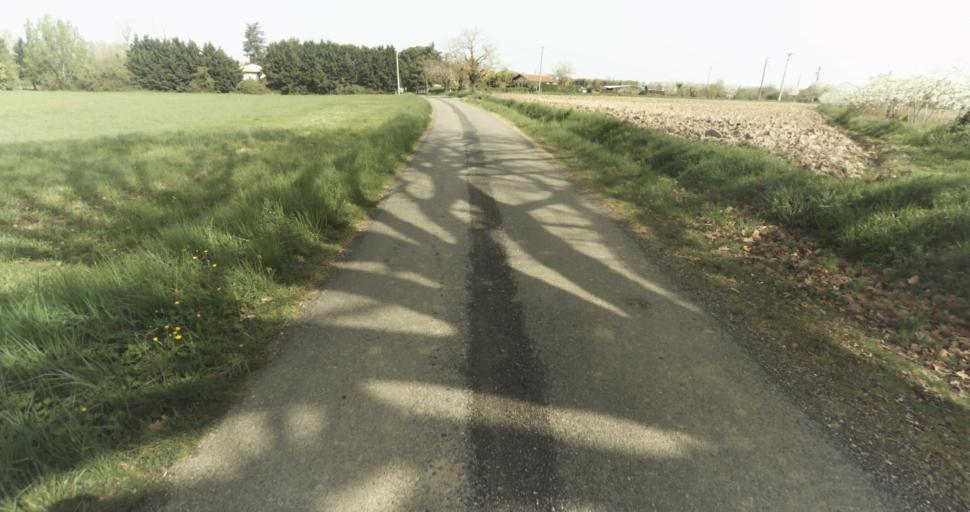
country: FR
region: Midi-Pyrenees
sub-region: Departement du Tarn-et-Garonne
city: Moissac
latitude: 44.0821
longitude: 1.0936
